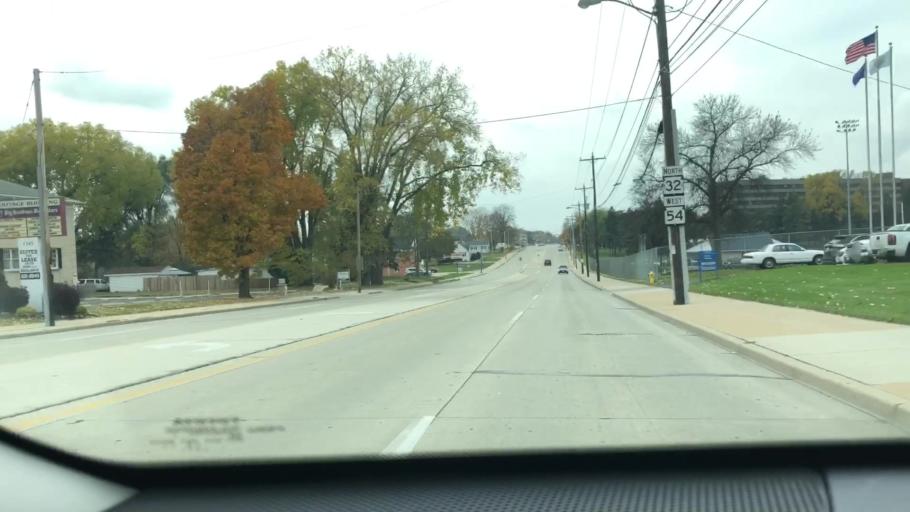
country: US
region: Wisconsin
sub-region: Brown County
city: Green Bay
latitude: 44.5202
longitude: -88.0540
